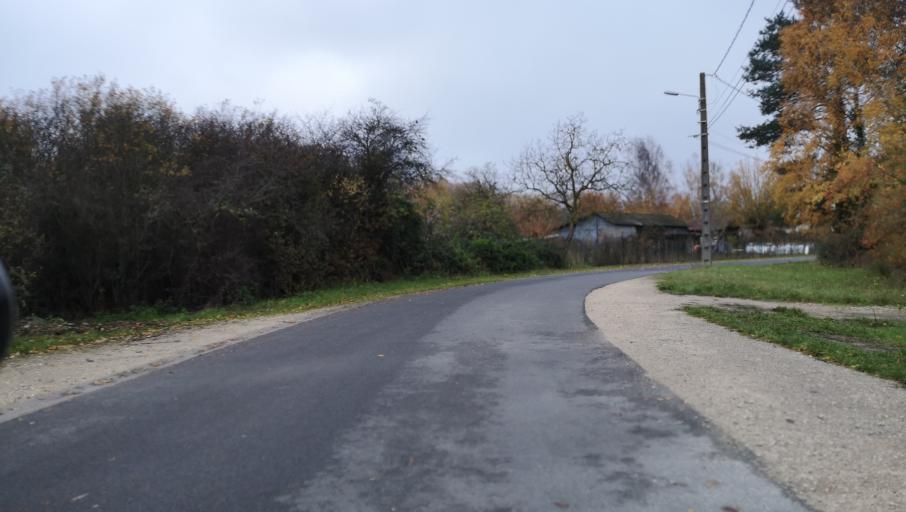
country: FR
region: Centre
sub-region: Departement du Loiret
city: Semoy
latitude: 47.9213
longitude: 1.9360
